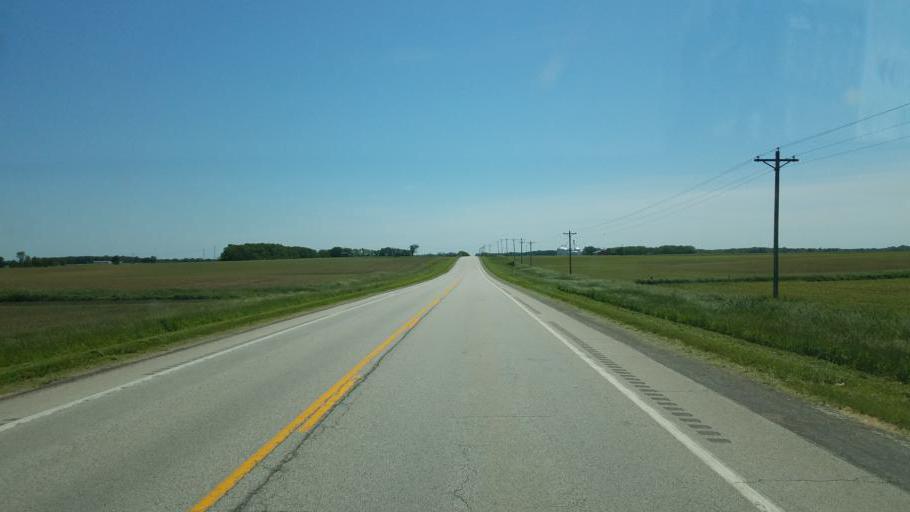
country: US
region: Illinois
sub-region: McLean County
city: Le Roy
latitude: 40.3118
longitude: -88.7993
